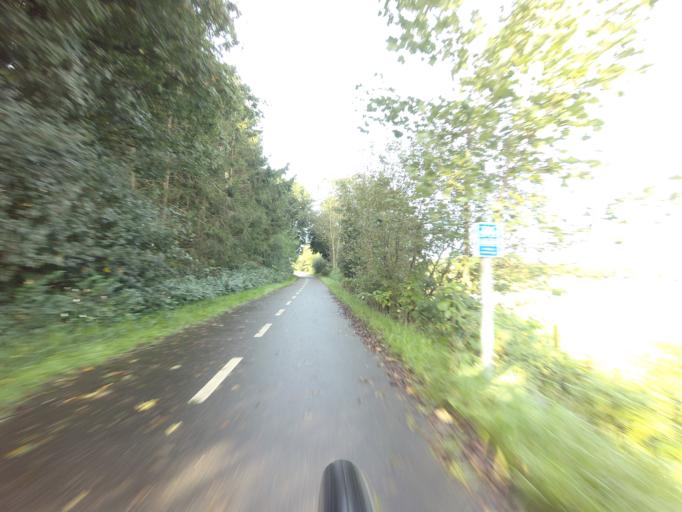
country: DK
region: Central Jutland
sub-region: Viborg Kommune
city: Viborg
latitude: 56.4282
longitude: 9.4153
